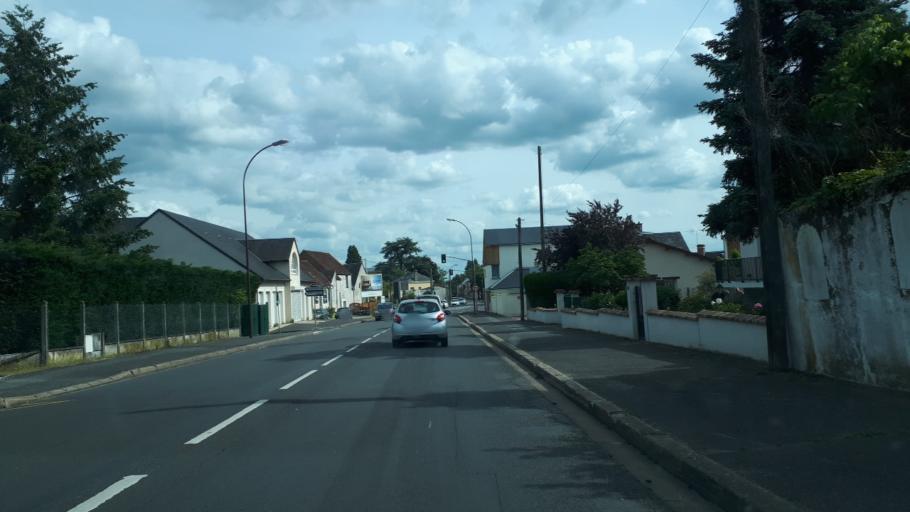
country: FR
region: Centre
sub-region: Departement du Loir-et-Cher
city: Romorantin-Lanthenay
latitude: 47.3609
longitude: 1.7393
